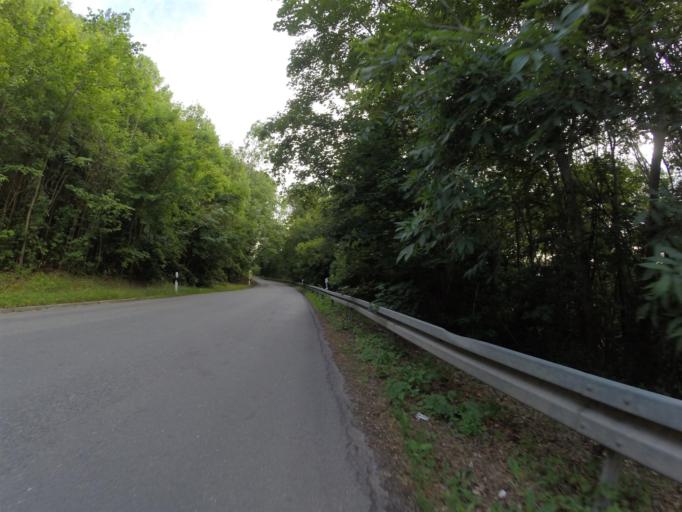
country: DE
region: Thuringia
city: Neuengonna
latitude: 50.9640
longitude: 11.6448
